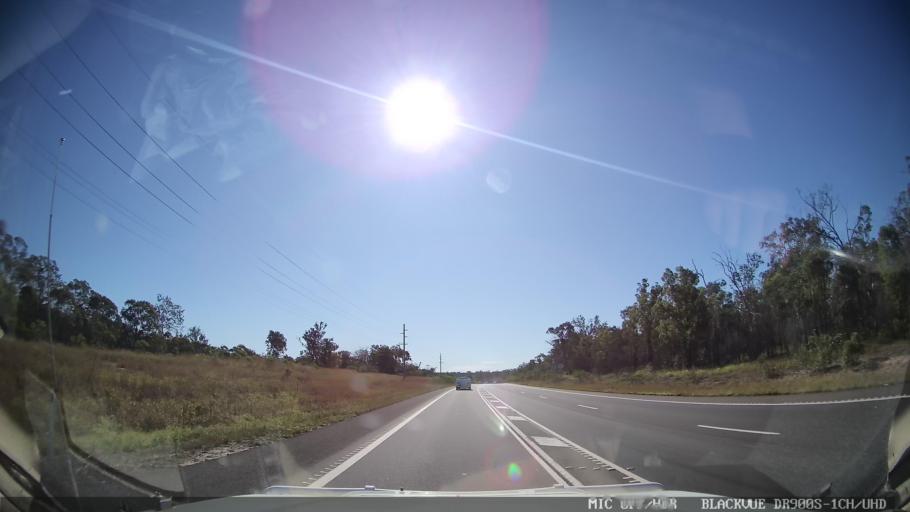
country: AU
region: Queensland
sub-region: Bundaberg
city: Childers
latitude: -25.2716
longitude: 152.3787
